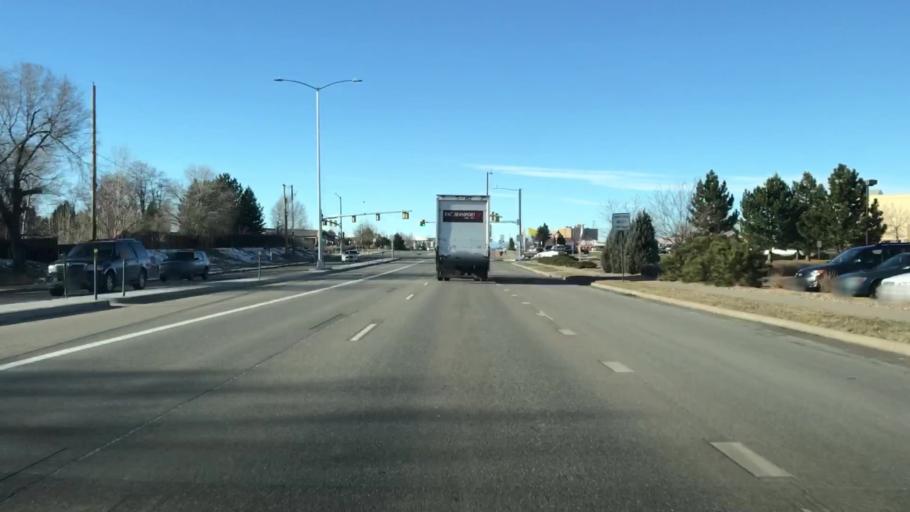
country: US
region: Colorado
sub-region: Arapahoe County
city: Glendale
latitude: 39.6885
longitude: -104.8883
